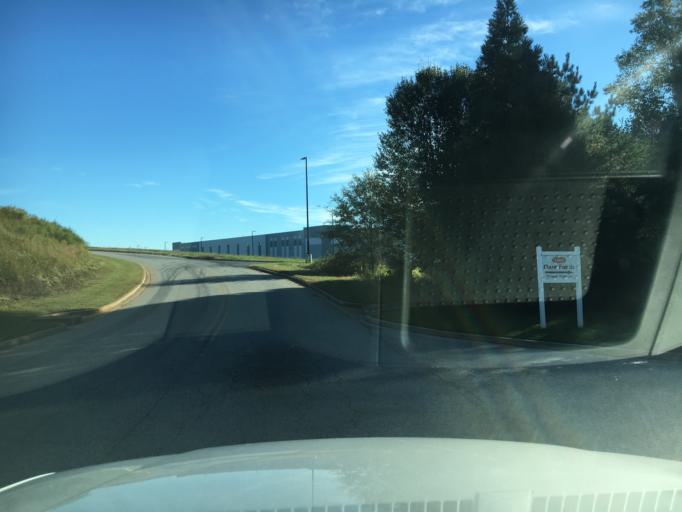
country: US
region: South Carolina
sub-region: Spartanburg County
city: Wellford
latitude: 34.9056
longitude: -82.0894
